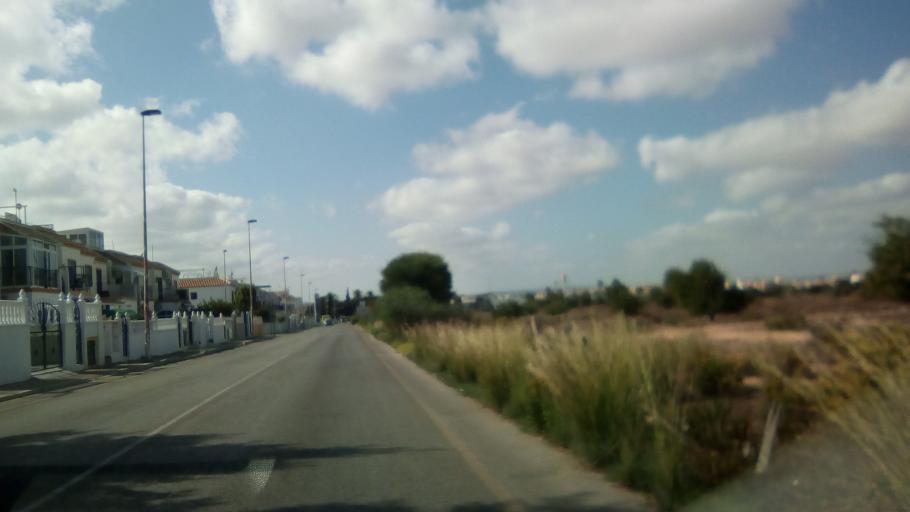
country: ES
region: Valencia
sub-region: Provincia de Alicante
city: Torrevieja
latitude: 38.0008
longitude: -0.6875
